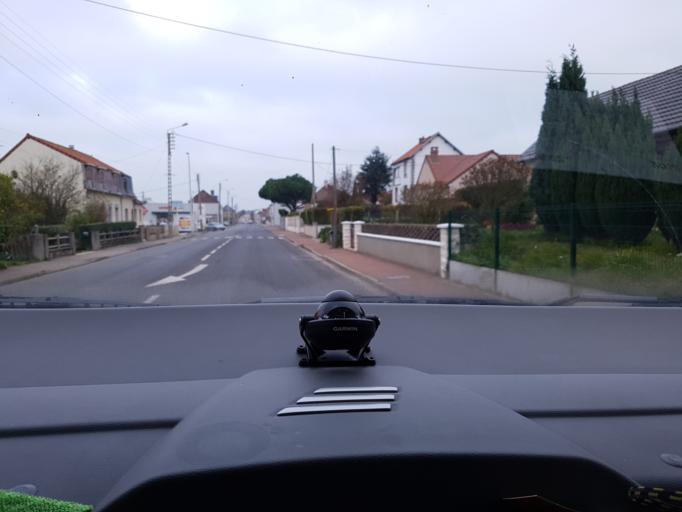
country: FR
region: Picardie
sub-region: Departement de la Somme
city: Mers-les-Bains
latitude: 50.0623
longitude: 1.4037
